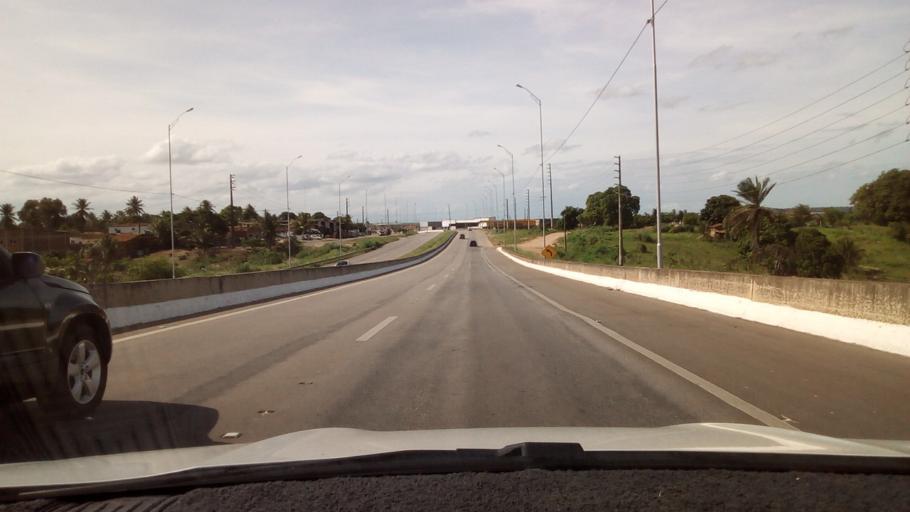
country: BR
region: Paraiba
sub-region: Bayeux
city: Bayeux
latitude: -7.1208
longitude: -34.9482
